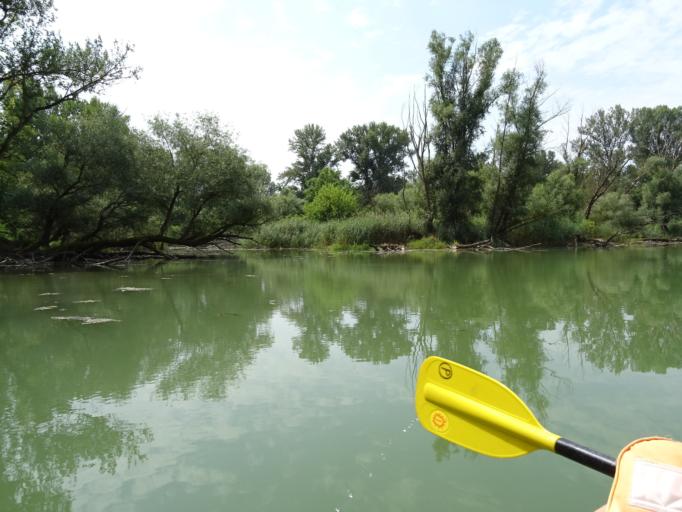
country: HU
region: Gyor-Moson-Sopron
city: Halaszi
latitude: 47.9599
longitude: 17.3834
